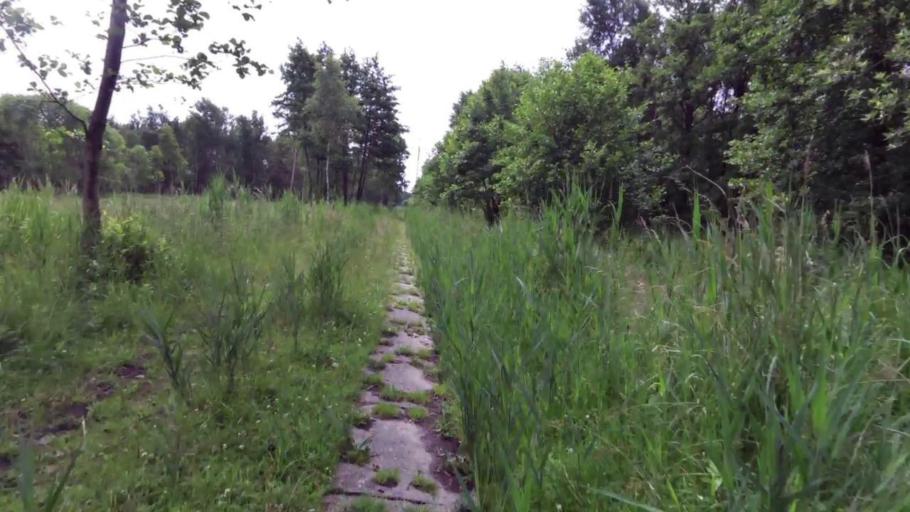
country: PL
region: West Pomeranian Voivodeship
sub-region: Powiat goleniowski
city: Stepnica
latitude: 53.7358
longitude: 14.6018
